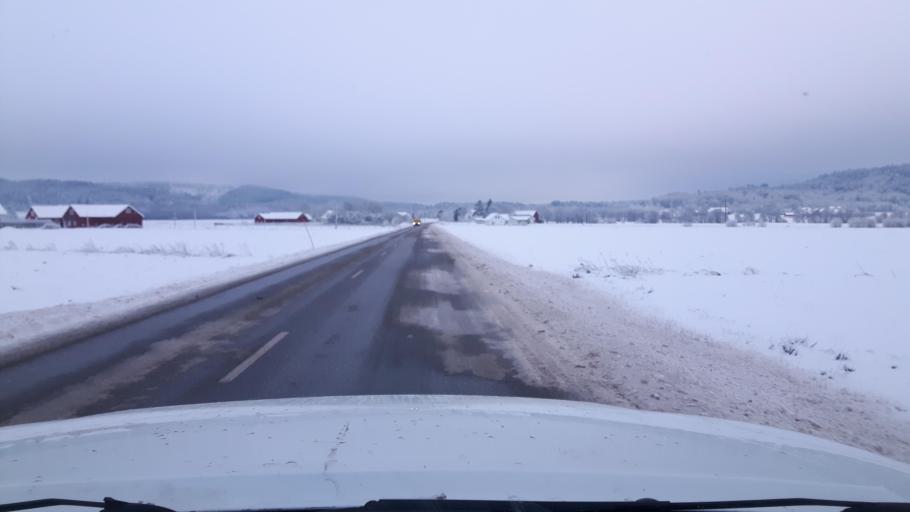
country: SE
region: Halland
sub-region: Kungsbacka Kommun
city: Fjaeras kyrkby
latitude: 57.4278
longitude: 12.1916
